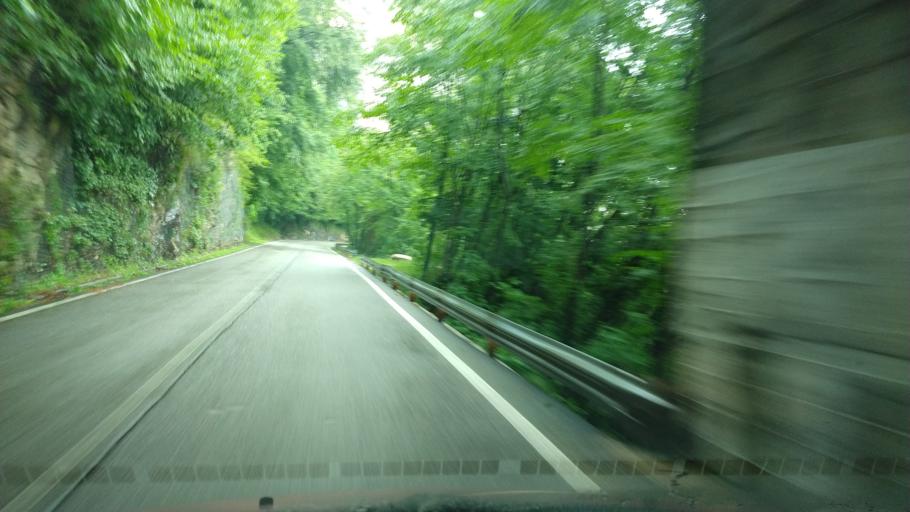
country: IT
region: Veneto
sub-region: Provincia di Vicenza
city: Tonezza del Cimone
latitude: 45.8427
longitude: 11.3611
